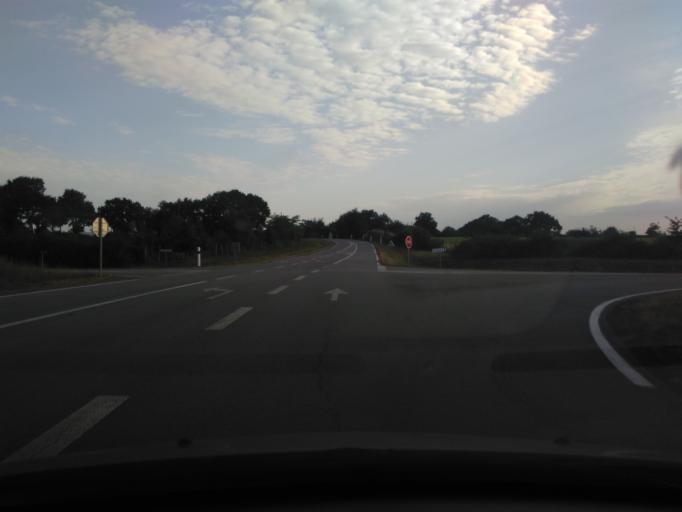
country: FR
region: Pays de la Loire
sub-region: Departement de la Vendee
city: Nesmy
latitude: 46.6266
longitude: -1.4062
